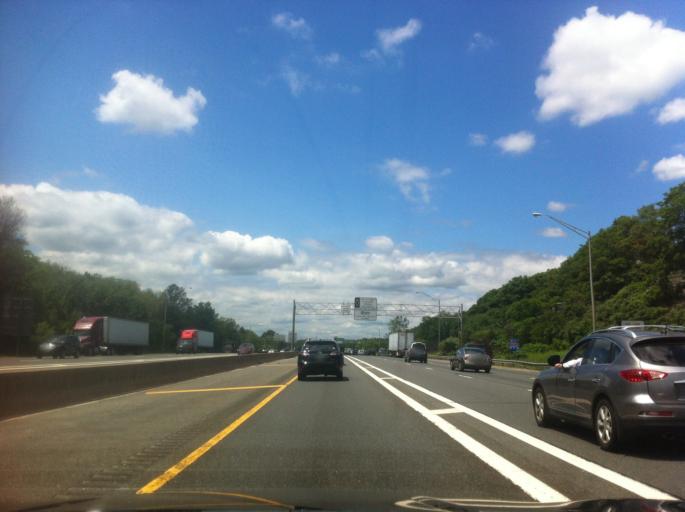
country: US
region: New York
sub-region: Suffolk County
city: Dix Hills
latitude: 40.8042
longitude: -73.3045
